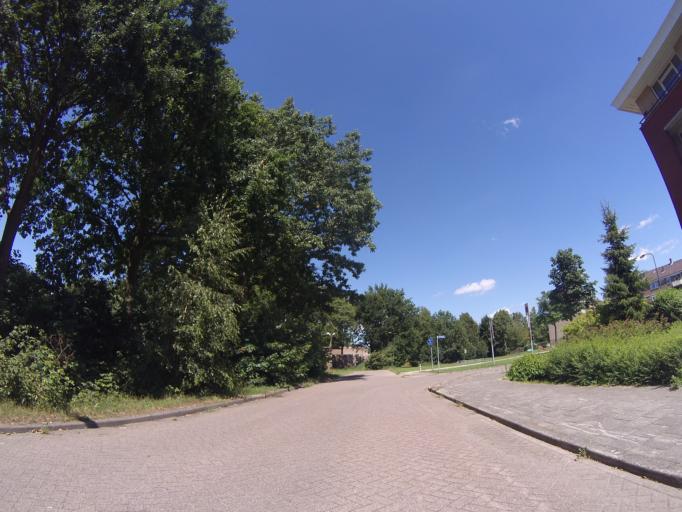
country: NL
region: Utrecht
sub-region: Gemeente De Bilt
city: De Bilt
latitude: 52.1224
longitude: 5.1798
